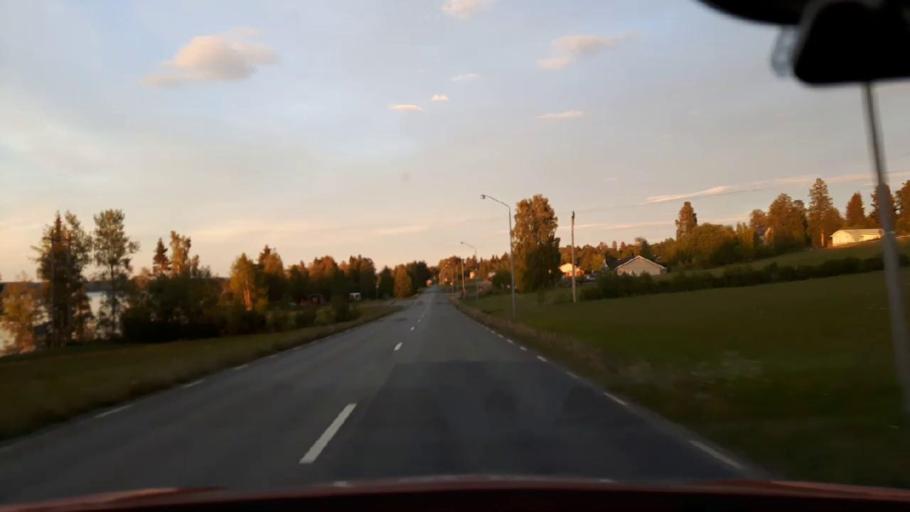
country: SE
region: Jaemtland
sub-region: OEstersunds Kommun
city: Ostersund
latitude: 63.1359
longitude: 14.6395
